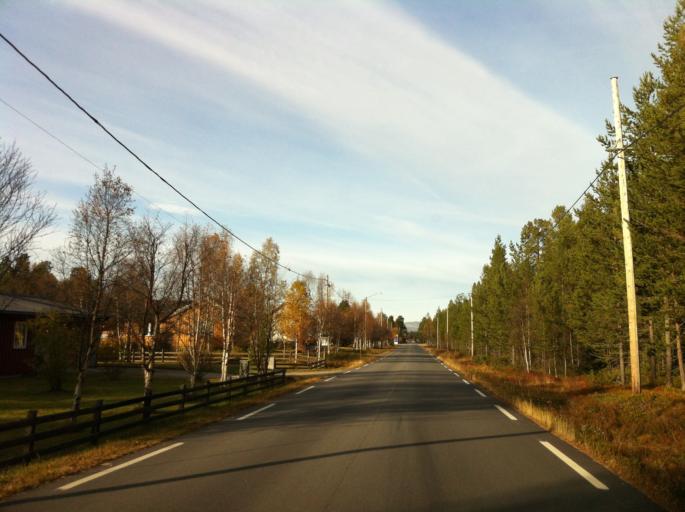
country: NO
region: Hedmark
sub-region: Engerdal
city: Engerdal
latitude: 62.1493
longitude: 11.9528
